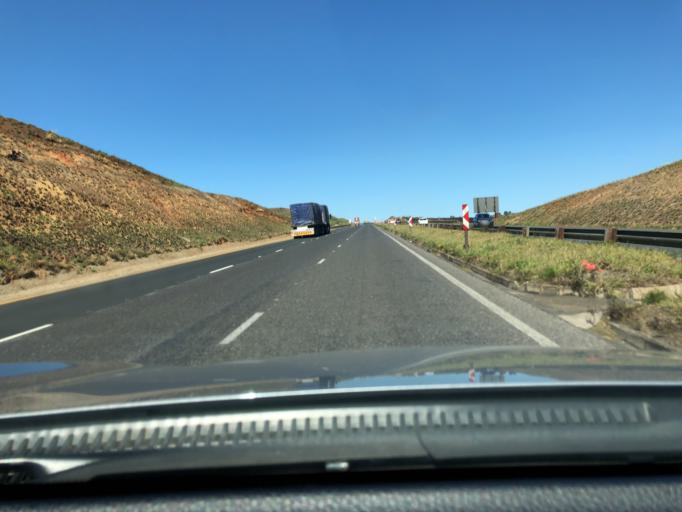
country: ZA
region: KwaZulu-Natal
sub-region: uMgungundlovu District Municipality
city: Howick
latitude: -29.4301
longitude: 30.1717
